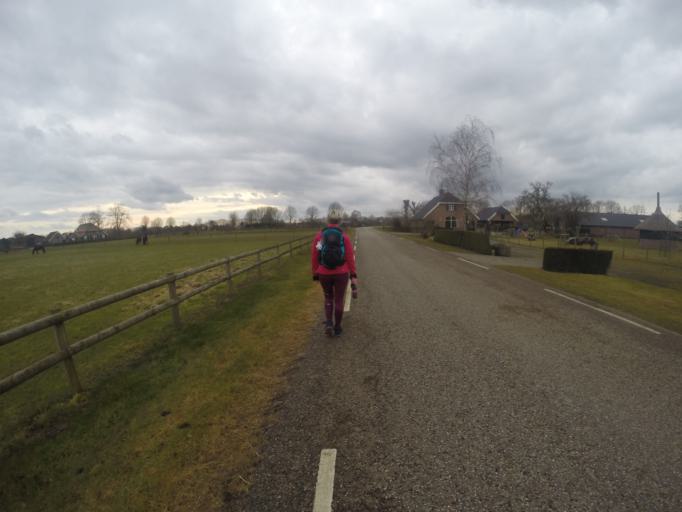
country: NL
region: Gelderland
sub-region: Gemeente Bronckhorst
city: Hengelo
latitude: 52.0488
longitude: 6.3317
